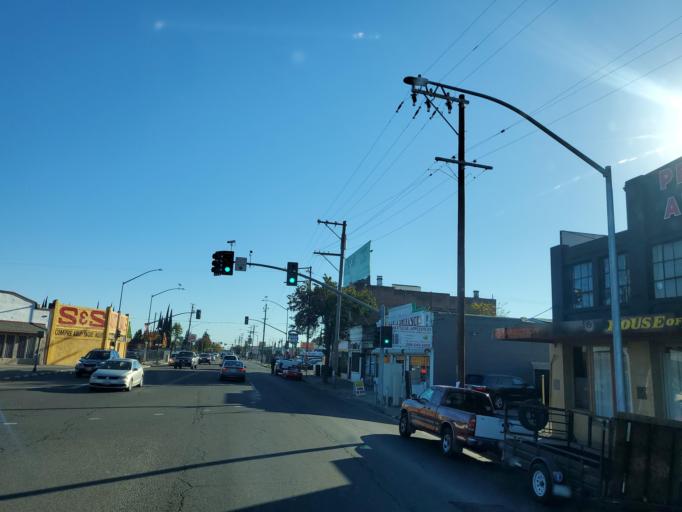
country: US
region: California
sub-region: San Joaquin County
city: August
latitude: 37.9654
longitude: -121.2742
